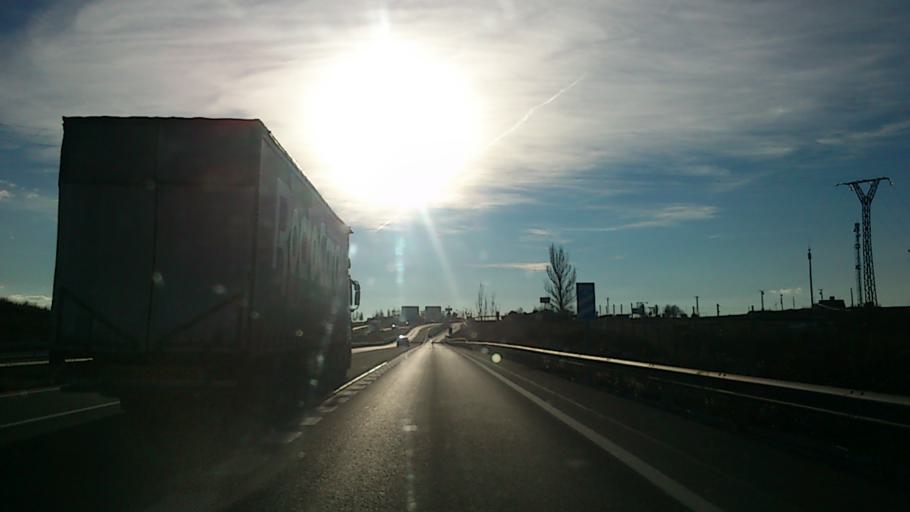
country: ES
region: Castille-La Mancha
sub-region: Provincia de Guadalajara
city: Almadrones
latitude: 40.9024
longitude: -2.7520
